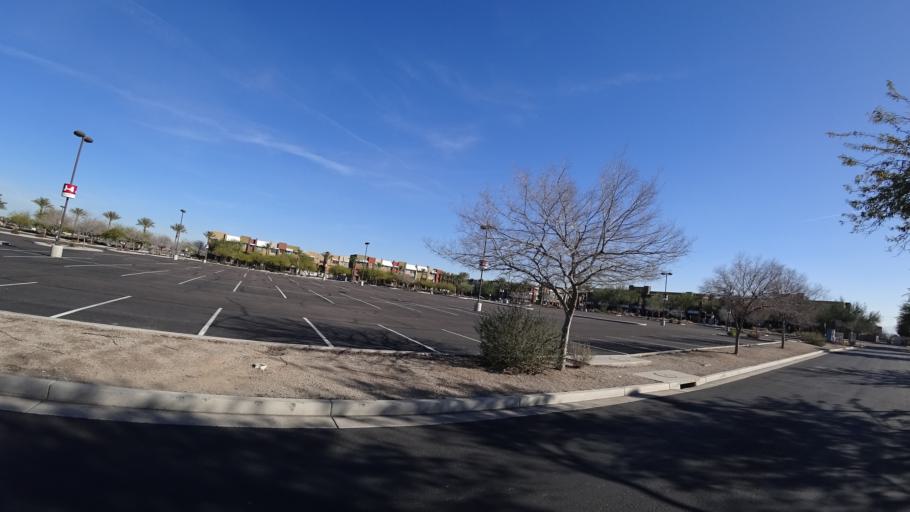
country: US
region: Arizona
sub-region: Maricopa County
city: Peoria
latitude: 33.5343
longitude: -112.2589
